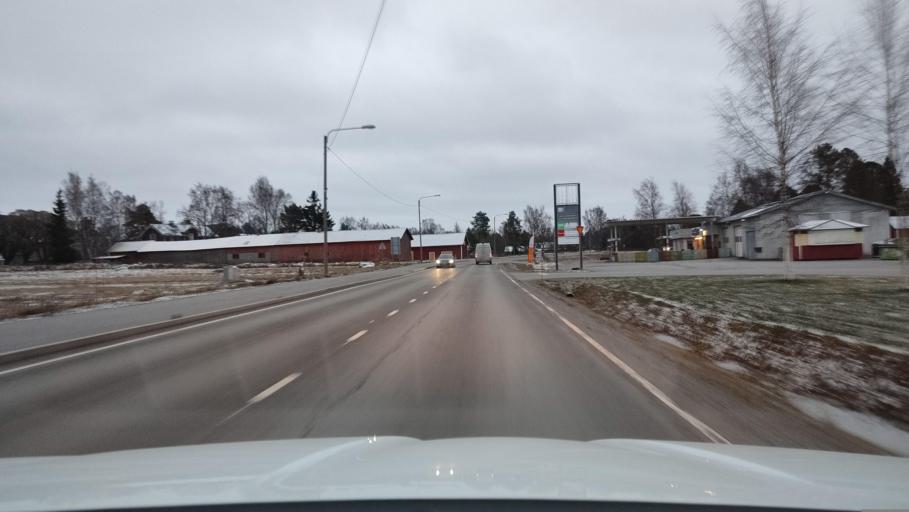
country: FI
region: Ostrobothnia
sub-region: Vaasa
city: Replot
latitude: 63.2318
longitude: 21.4091
